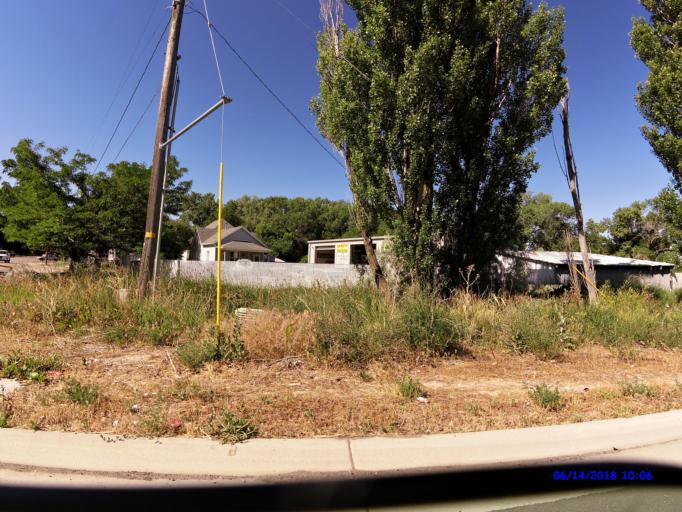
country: US
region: Utah
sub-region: Weber County
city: Ogden
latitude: 41.2257
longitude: -111.9927
